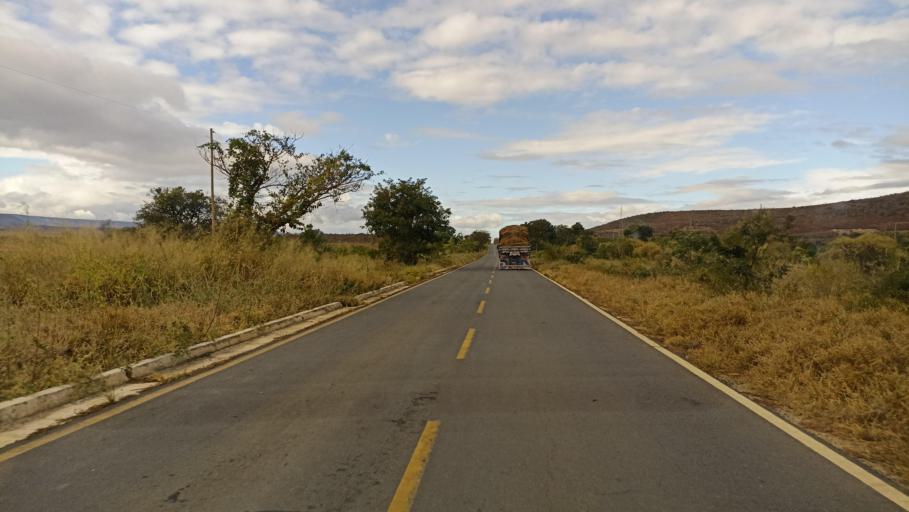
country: BR
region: Minas Gerais
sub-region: Itinga
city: Itinga
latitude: -16.5957
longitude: -41.7012
